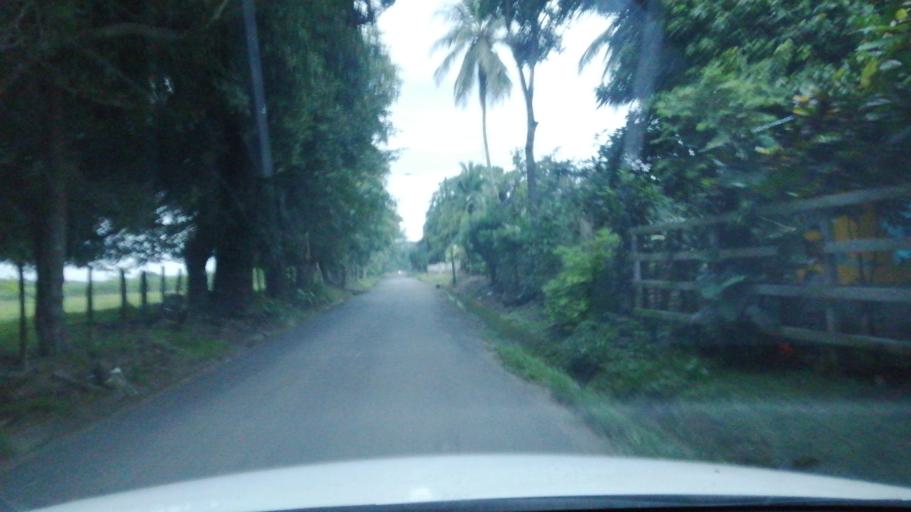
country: PA
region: Chiriqui
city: Alanje
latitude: 8.4014
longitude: -82.4987
